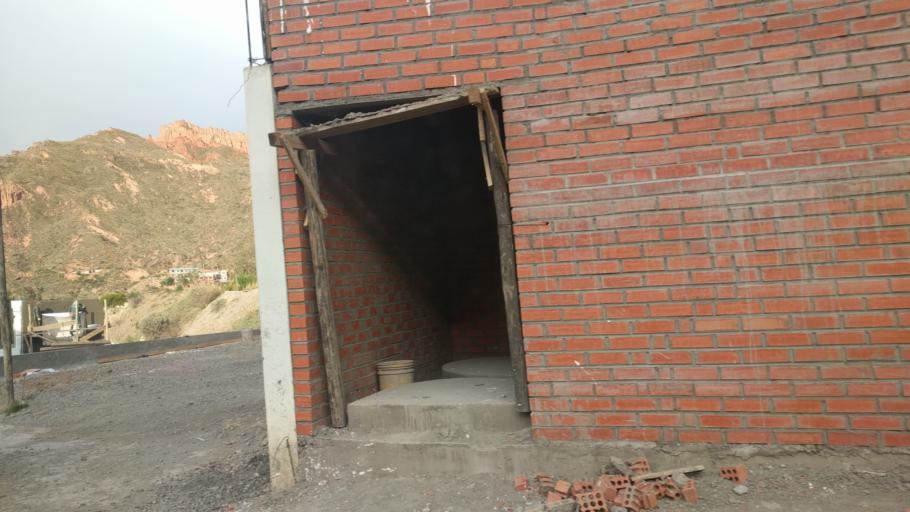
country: BO
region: La Paz
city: La Paz
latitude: -16.5616
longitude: -68.0964
